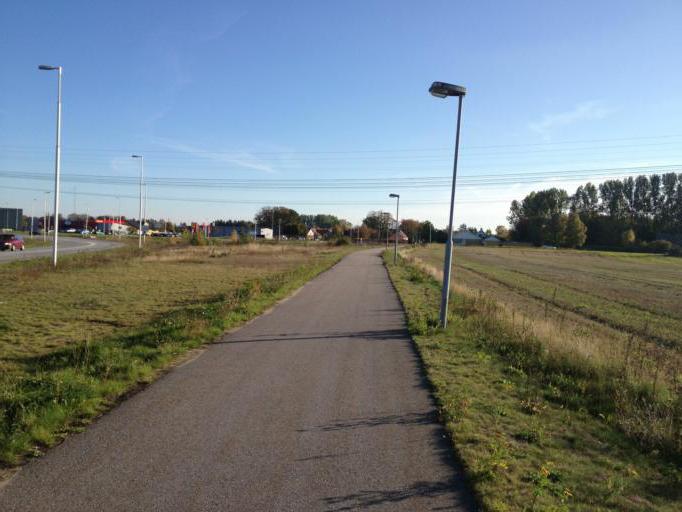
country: SE
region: Skane
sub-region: Kavlinge Kommun
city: Loddekopinge
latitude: 55.7424
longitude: 13.0300
